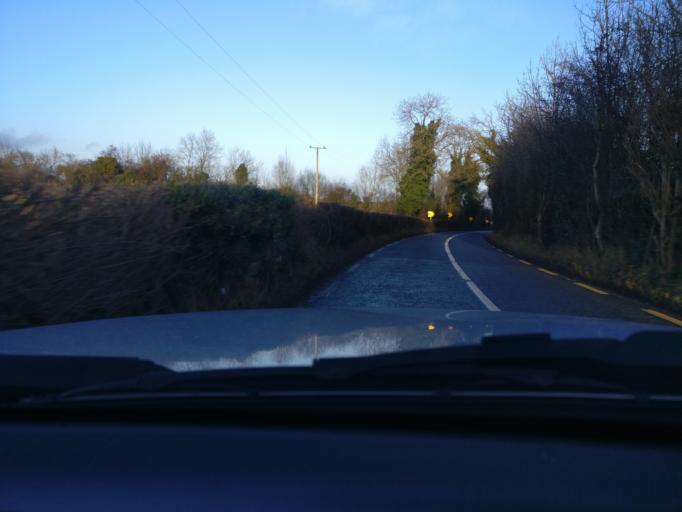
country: IE
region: Ulster
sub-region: An Cabhan
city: Kingscourt
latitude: 53.7908
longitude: -6.7272
